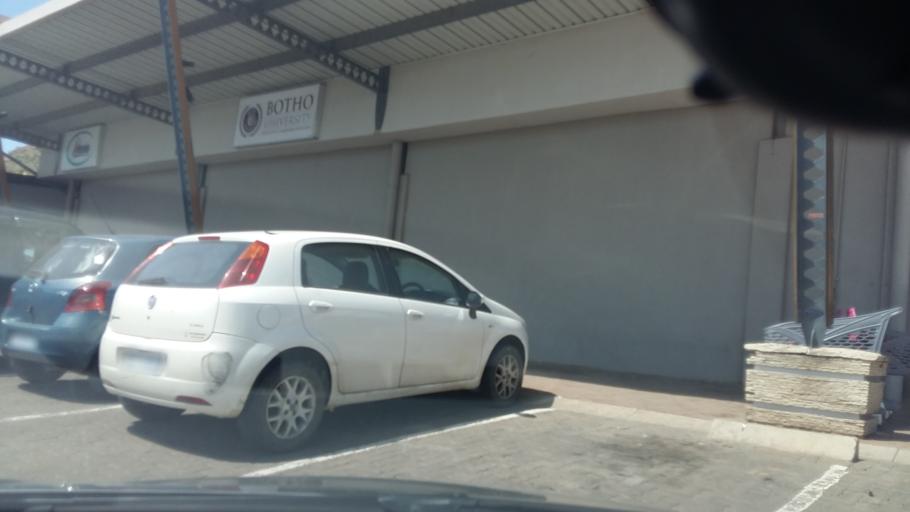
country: LS
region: Maseru
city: Maseru
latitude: -29.3354
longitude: 27.4821
